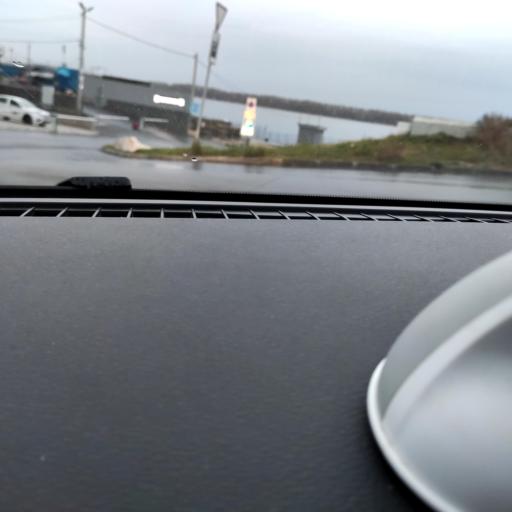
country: RU
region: Samara
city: Rozhdestveno
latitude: 53.1834
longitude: 50.0755
